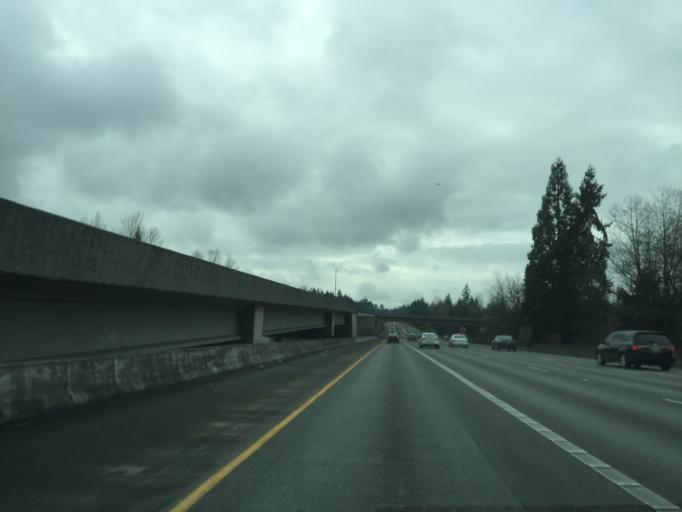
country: US
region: Washington
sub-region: Snohomish County
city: Alderwood Manor
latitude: 47.8145
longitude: -122.2917
